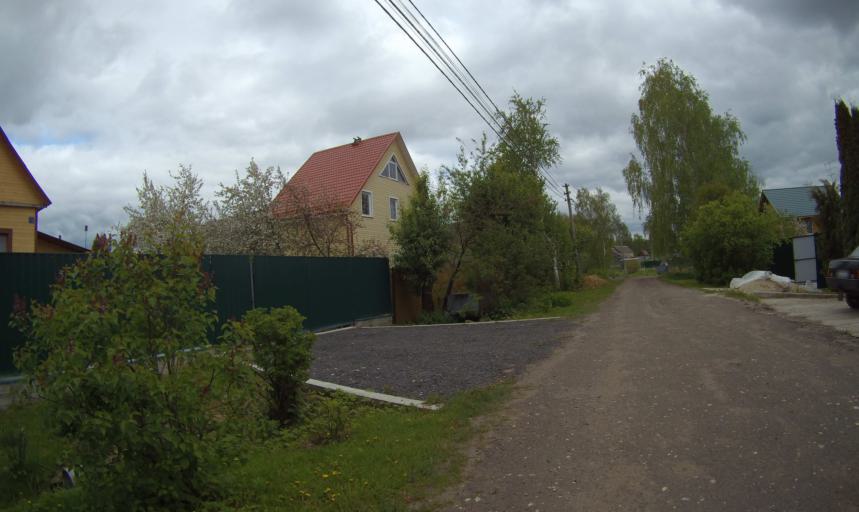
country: RU
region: Moskovskaya
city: Rechitsy
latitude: 55.5753
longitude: 38.5007
